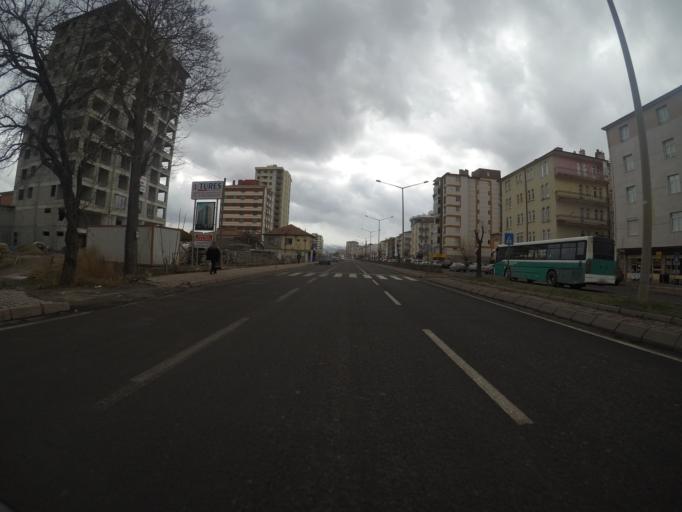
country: TR
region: Kayseri
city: Melikgazi
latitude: 38.7582
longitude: 35.4669
